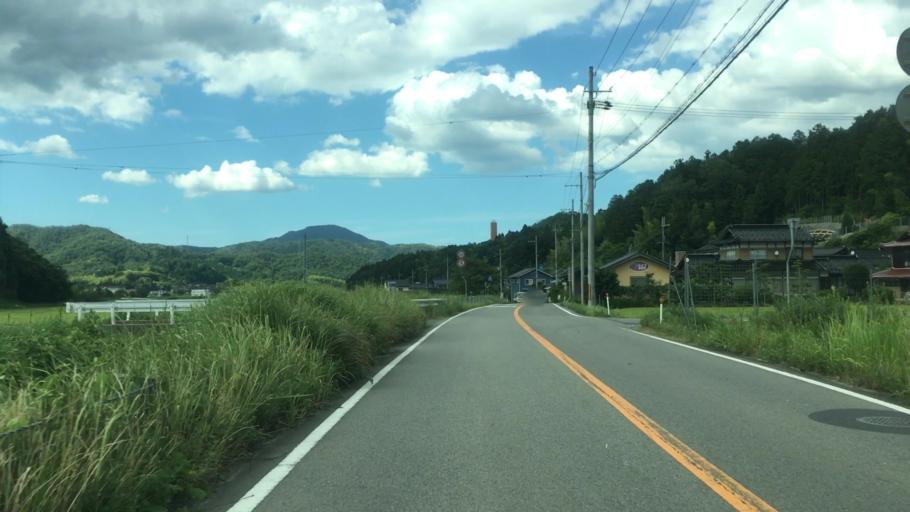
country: JP
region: Hyogo
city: Toyooka
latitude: 35.5389
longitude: 134.7900
